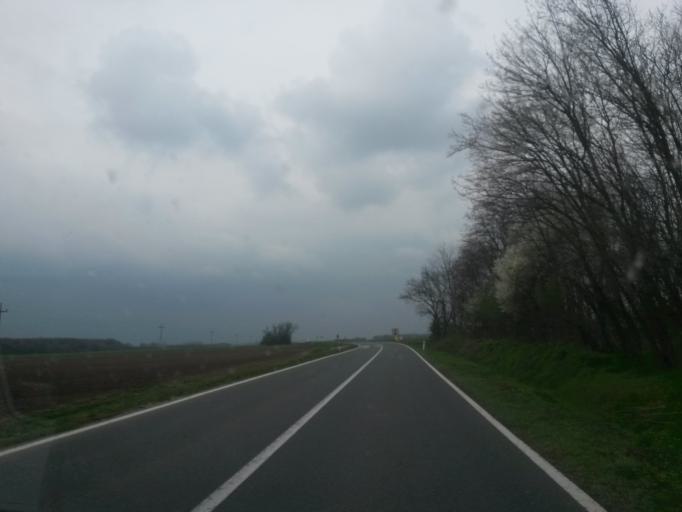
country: HR
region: Vukovarsko-Srijemska
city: Nijemci
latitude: 45.2001
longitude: 19.0149
